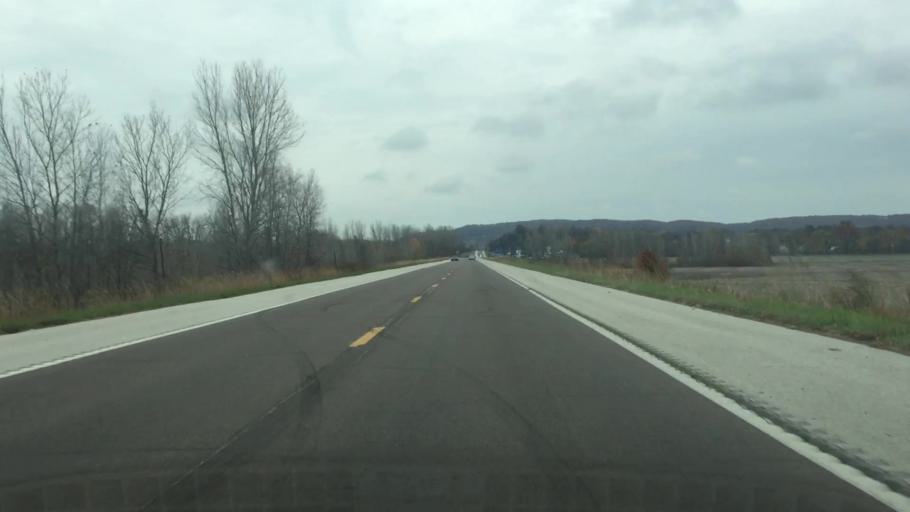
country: US
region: Missouri
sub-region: Gasconade County
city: Hermann
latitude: 38.7224
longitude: -91.4438
